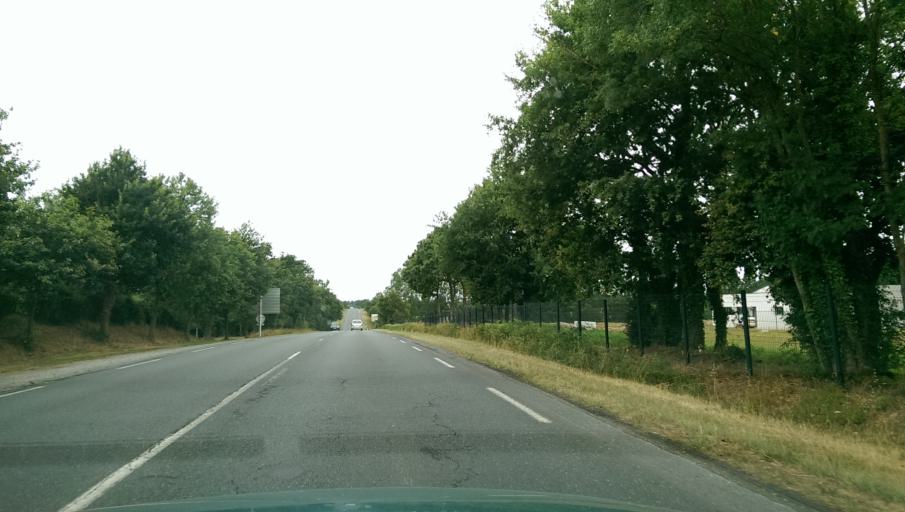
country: FR
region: Pays de la Loire
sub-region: Departement de la Loire-Atlantique
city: Remouille
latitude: 47.0590
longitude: -1.3765
